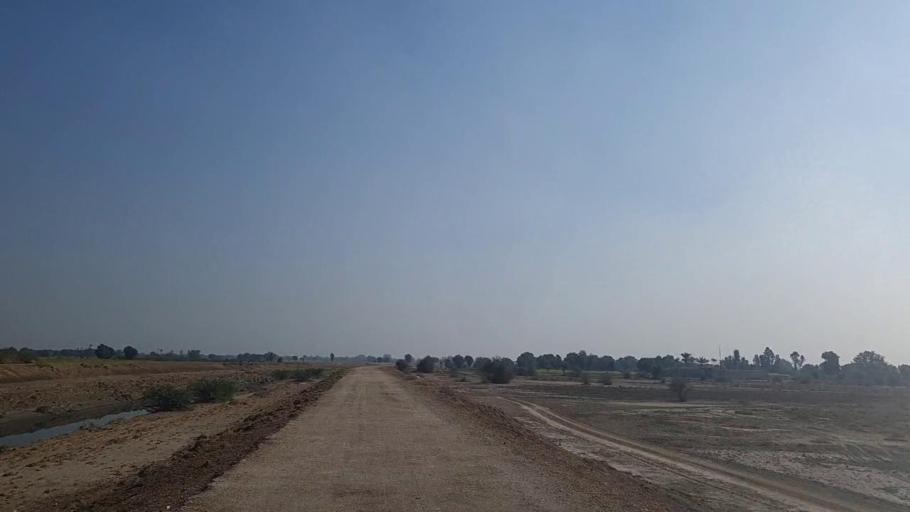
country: PK
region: Sindh
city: Shahpur Chakar
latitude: 26.1855
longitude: 68.5619
